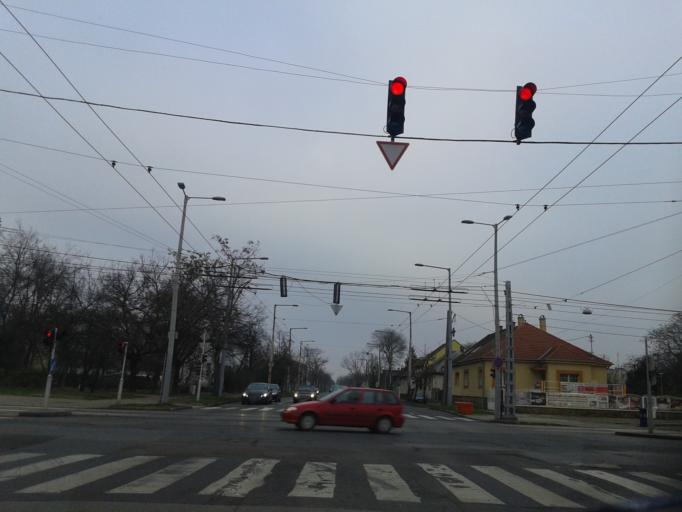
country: HU
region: Budapest
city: Budapest XIV. keruelet
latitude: 47.5092
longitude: 19.1289
